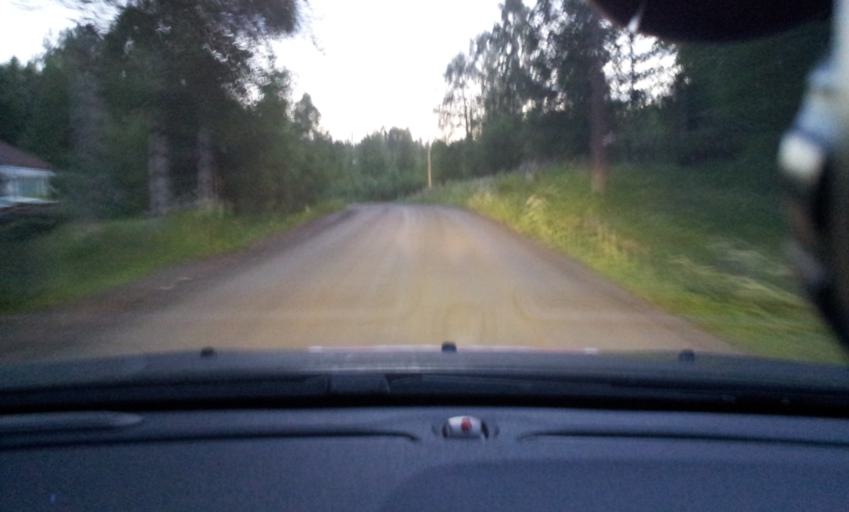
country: SE
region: Vaesternorrland
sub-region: Ange Kommun
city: Ange
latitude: 62.7697
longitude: 15.7530
